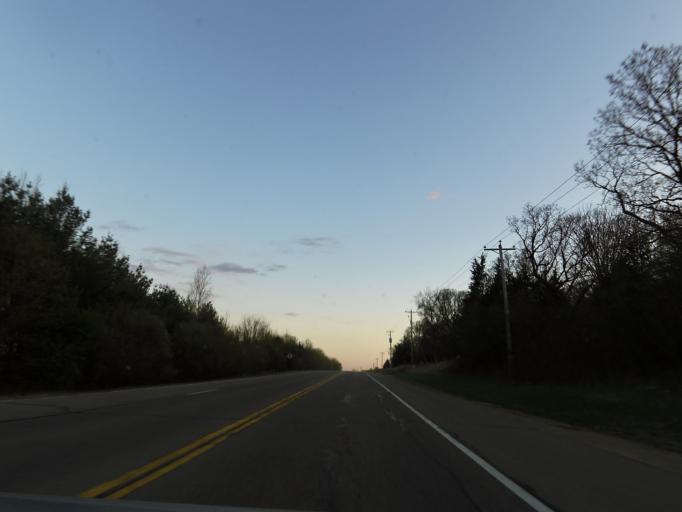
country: US
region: Minnesota
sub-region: Washington County
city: Lakeland
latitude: 44.9700
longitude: -92.7945
